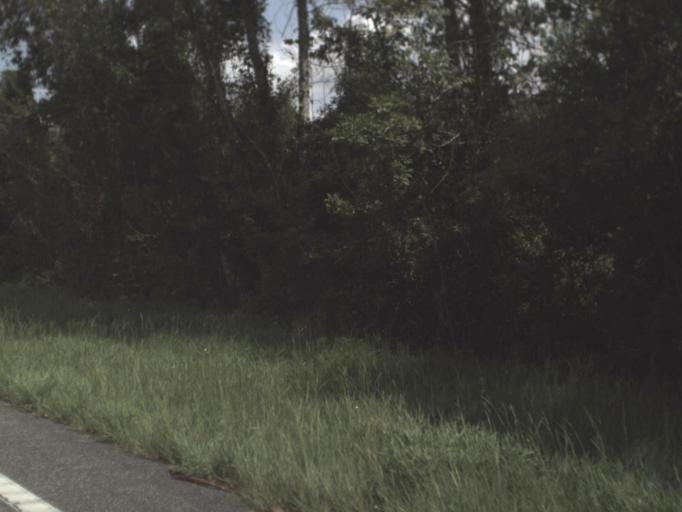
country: US
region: Florida
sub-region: Madison County
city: Madison
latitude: 30.4489
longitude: -83.3443
